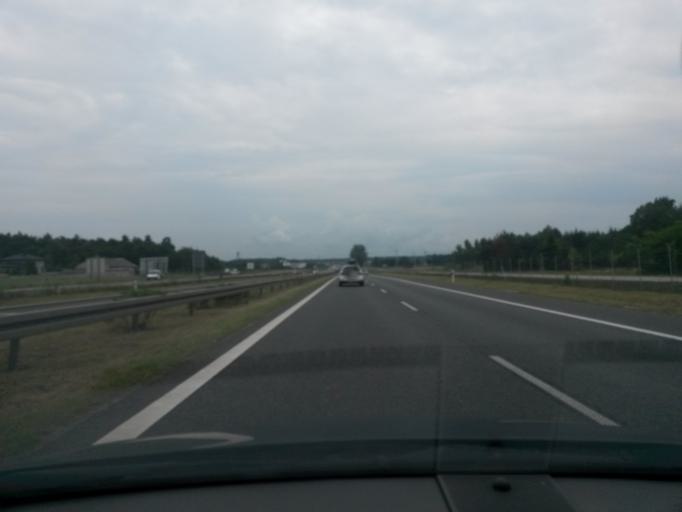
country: PL
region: Masovian Voivodeship
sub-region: Powiat zyrardowski
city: Mszczonow
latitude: 51.9484
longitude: 20.4882
